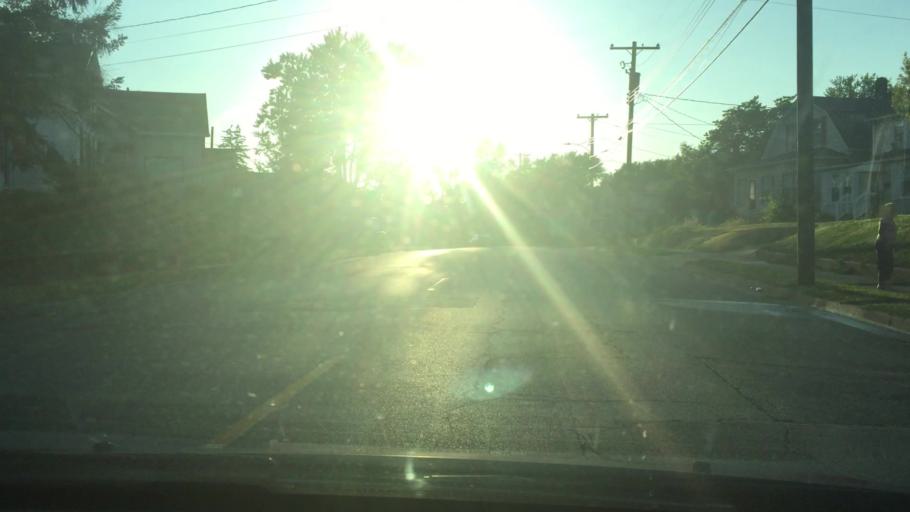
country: US
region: Iowa
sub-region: Muscatine County
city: Muscatine
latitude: 41.4195
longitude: -91.0605
